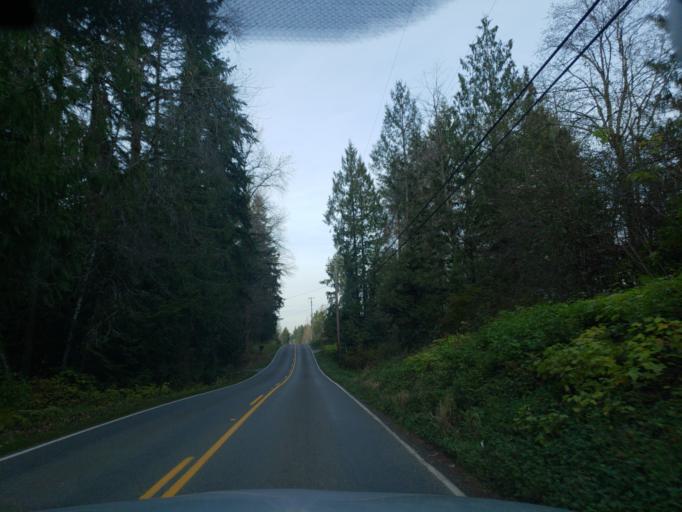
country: US
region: Washington
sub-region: Snohomish County
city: Cathcart
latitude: 47.8230
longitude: -122.0770
